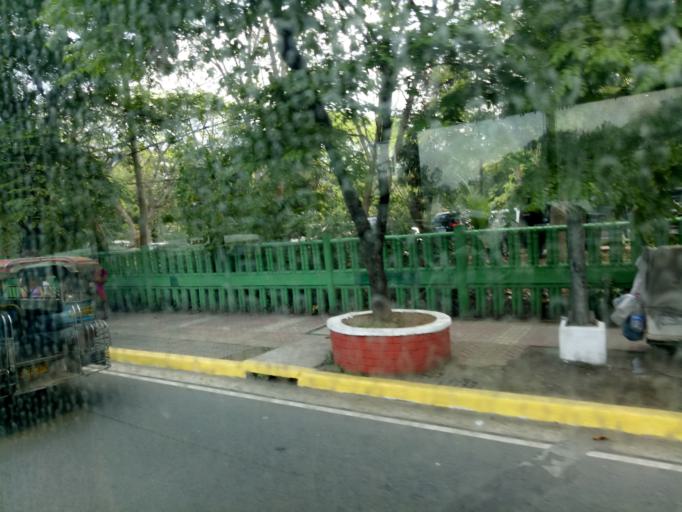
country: PH
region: Metro Manila
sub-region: Quezon City
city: Quezon City
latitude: 14.6486
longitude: 121.0483
